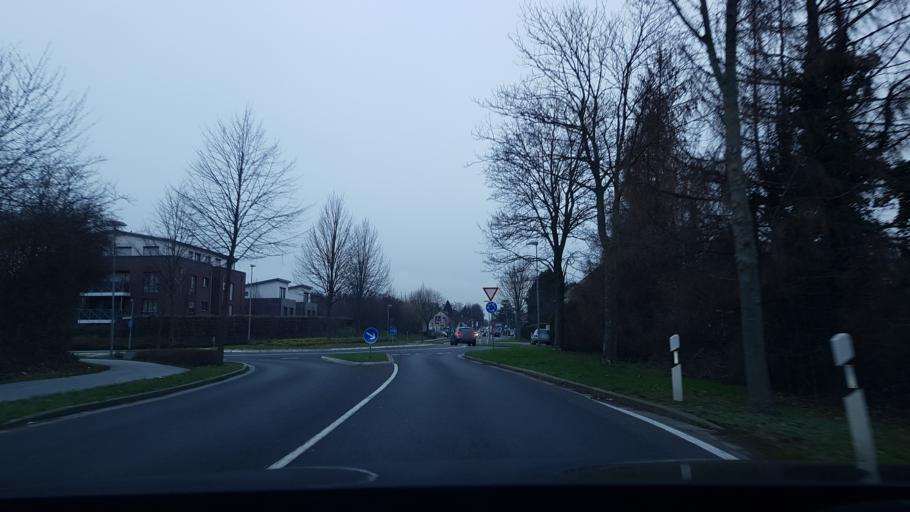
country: DE
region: North Rhine-Westphalia
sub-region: Regierungsbezirk Dusseldorf
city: Moers
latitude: 51.4188
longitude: 6.6564
